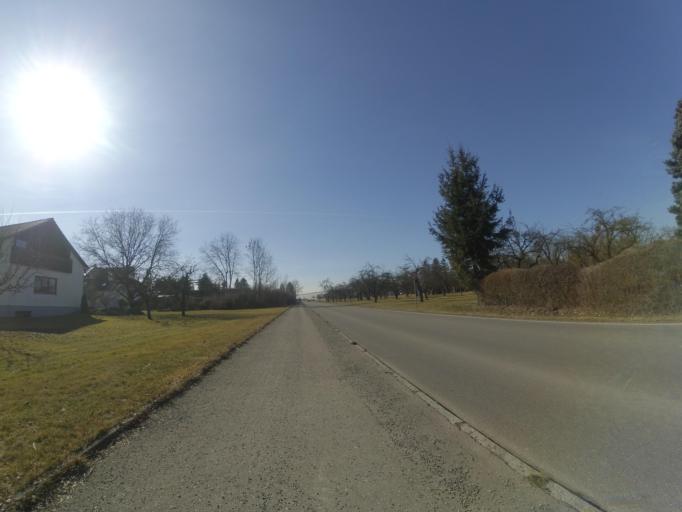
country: DE
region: Baden-Wuerttemberg
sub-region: Tuebingen Region
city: Baienfurt
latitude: 47.8392
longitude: 9.6398
